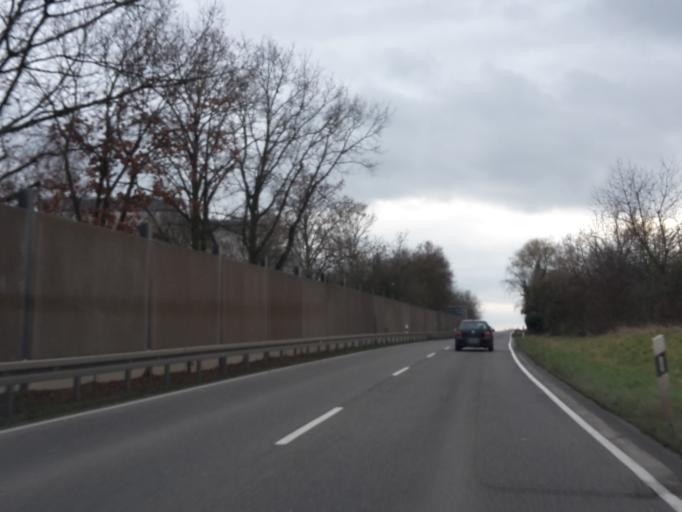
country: DE
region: Hesse
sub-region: Regierungsbezirk Darmstadt
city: Hochheim am Main
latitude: 50.0431
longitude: 8.3583
